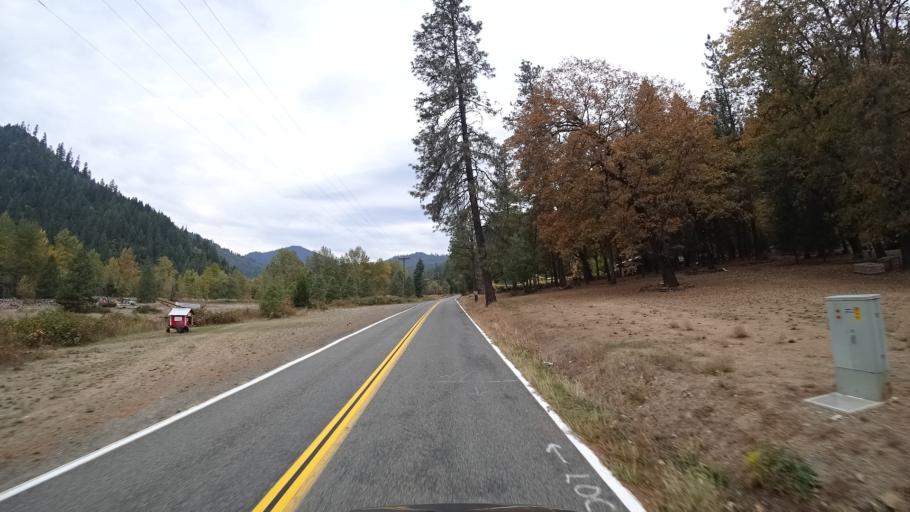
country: US
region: California
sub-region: Siskiyou County
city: Happy Camp
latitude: 41.8681
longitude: -123.4039
